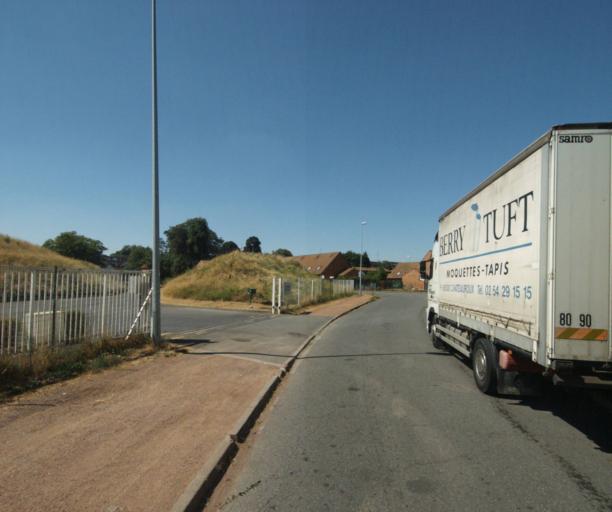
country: BE
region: Wallonia
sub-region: Province du Hainaut
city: Mouscron
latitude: 50.7315
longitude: 3.1874
